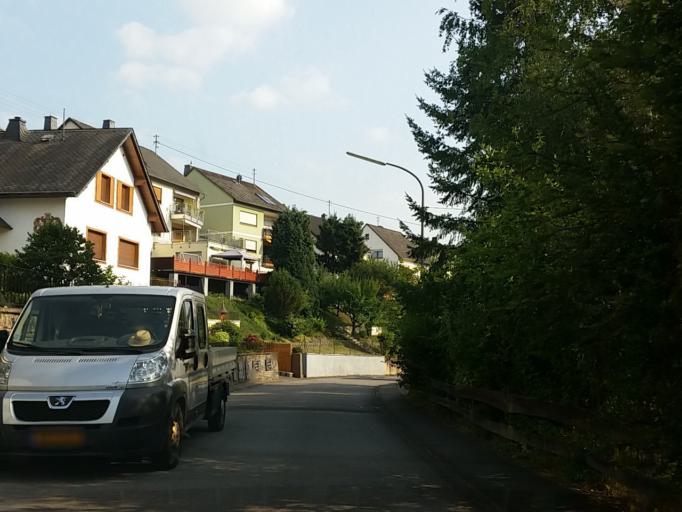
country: DE
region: Rheinland-Pfalz
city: Waldrach
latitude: 49.7475
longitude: 6.7443
